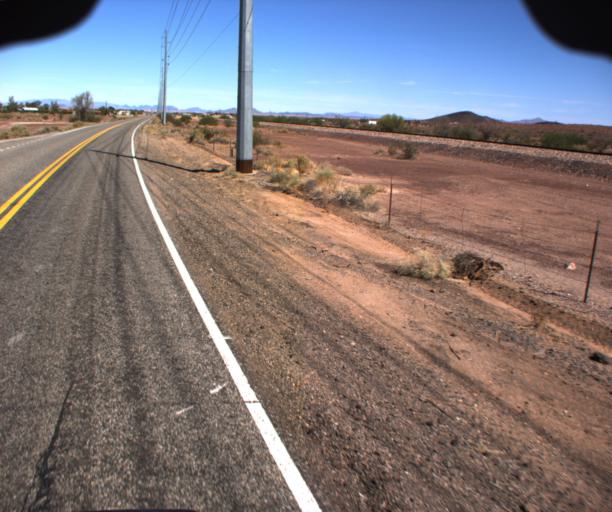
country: US
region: Arizona
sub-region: La Paz County
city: Quartzsite
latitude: 33.9137
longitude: -113.9912
